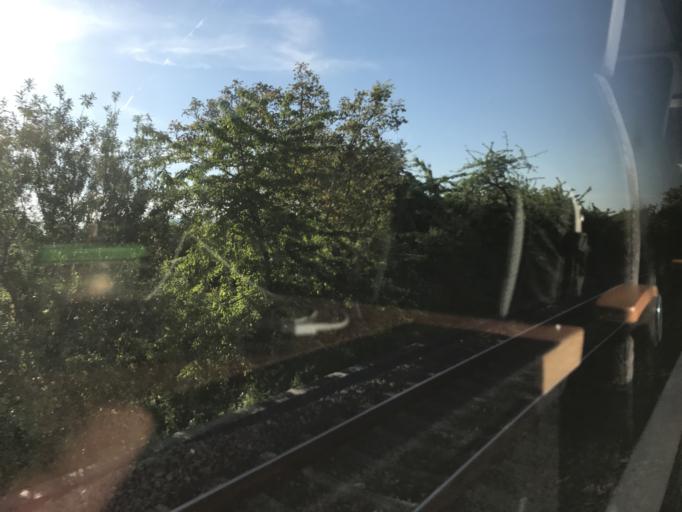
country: DE
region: Rheinland-Pfalz
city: Ockenheim
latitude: 49.9441
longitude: 7.9455
